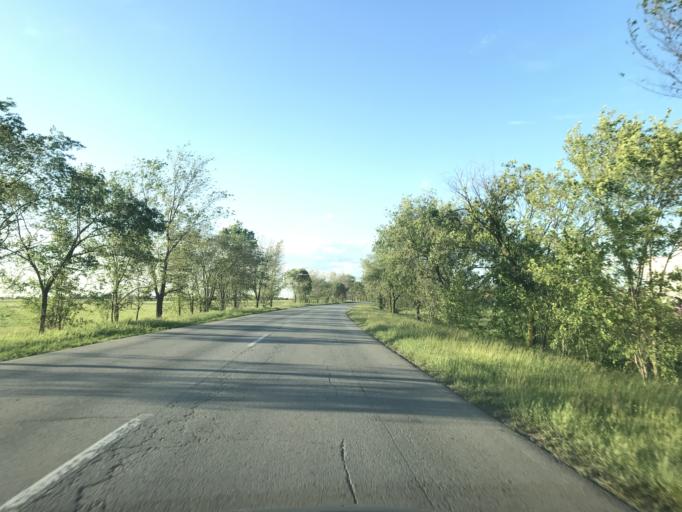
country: RS
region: Autonomna Pokrajina Vojvodina
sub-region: Srednjebanatski Okrug
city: Zrenjanin
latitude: 45.3893
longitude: 20.3525
